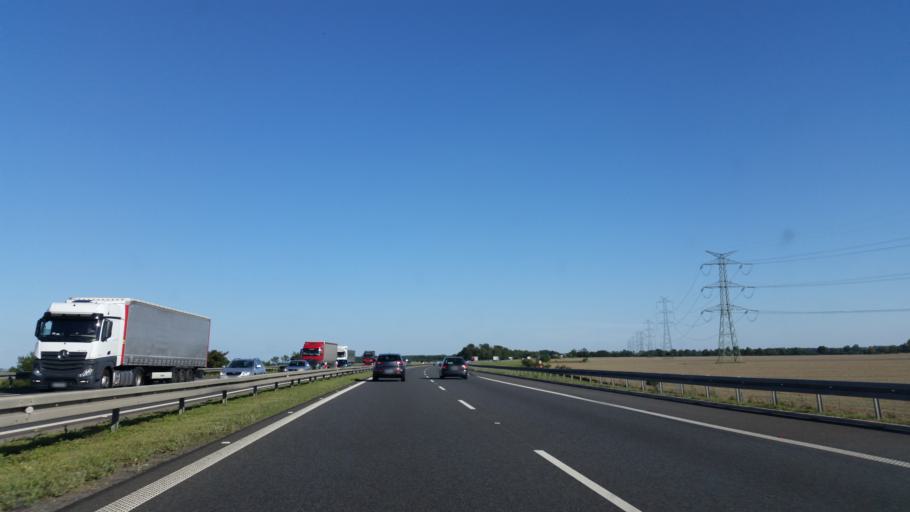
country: PL
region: Lower Silesian Voivodeship
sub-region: Powiat strzelinski
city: Wiazow
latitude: 50.8357
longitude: 17.2812
